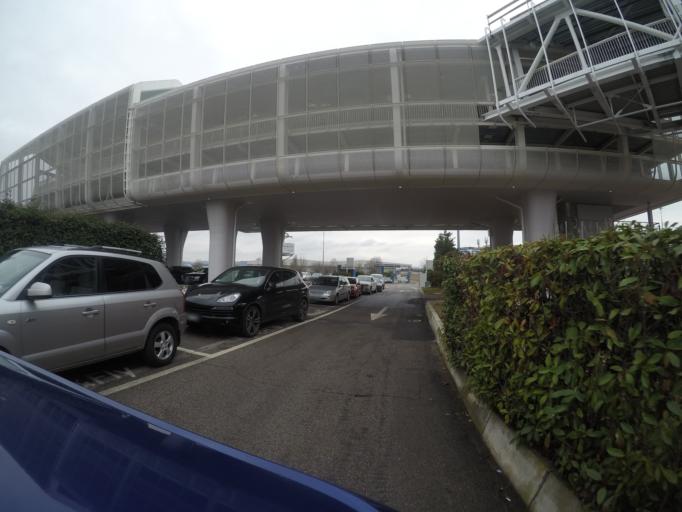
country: IT
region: Emilia-Romagna
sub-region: Provincia di Bologna
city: Trebbo
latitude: 44.5289
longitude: 11.2944
